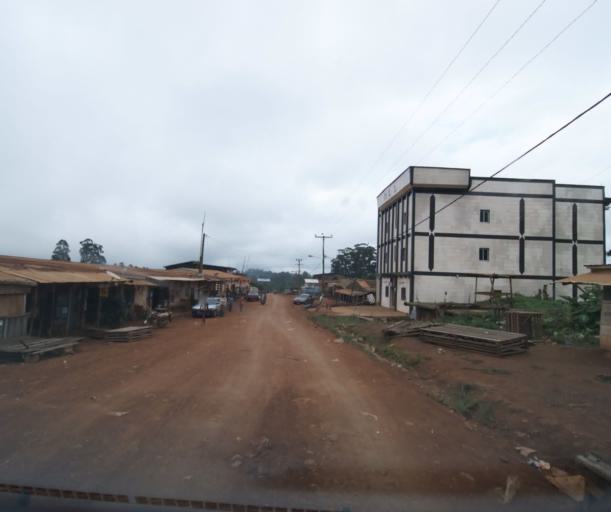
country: CM
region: West
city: Dschang
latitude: 5.5088
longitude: 9.9926
